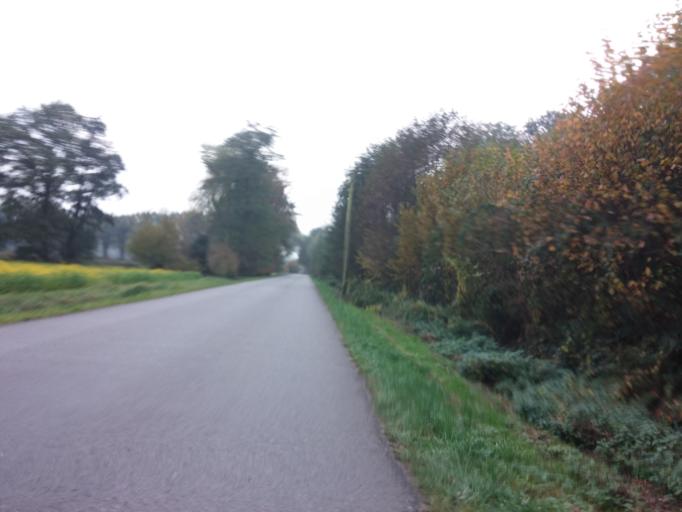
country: DE
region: North Rhine-Westphalia
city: Dorsten
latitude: 51.6379
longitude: 6.9790
